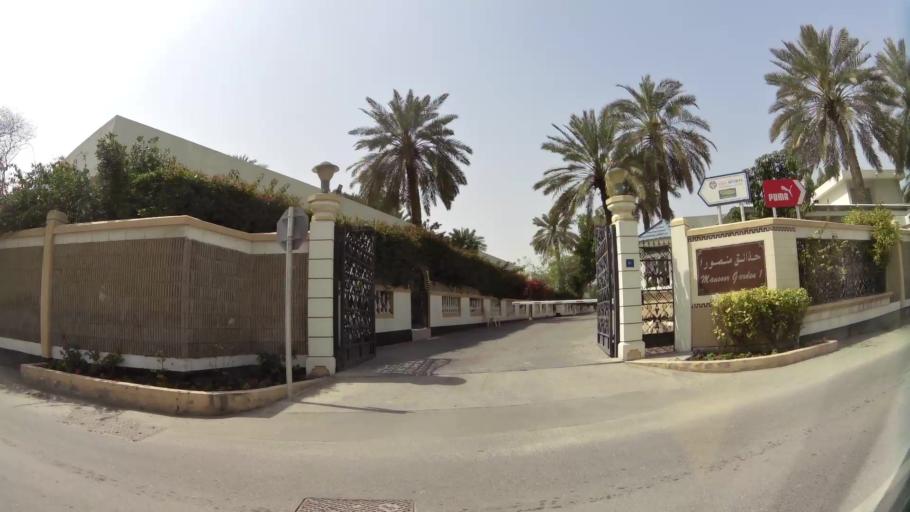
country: BH
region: Manama
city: Jidd Hafs
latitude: 26.2241
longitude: 50.4971
